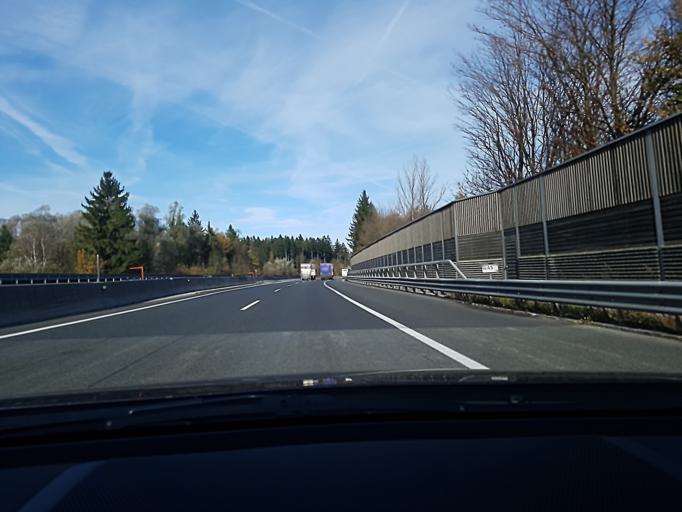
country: AT
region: Salzburg
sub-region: Politischer Bezirk Hallein
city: Adnet
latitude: 47.6578
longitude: 13.1329
